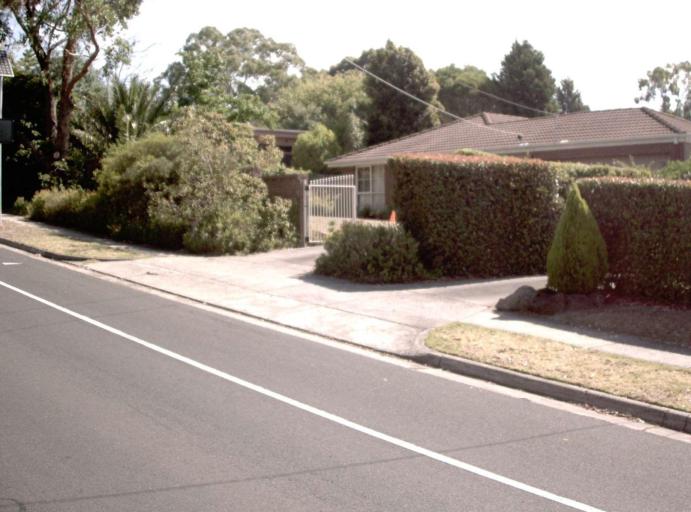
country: AU
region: Victoria
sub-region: Monash
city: Mulgrave
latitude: -37.8971
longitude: 145.1909
